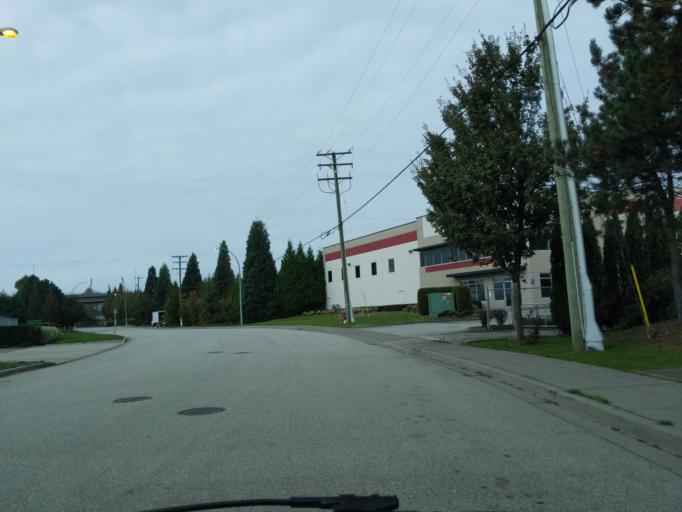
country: CA
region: British Columbia
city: Walnut Grove
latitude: 49.1874
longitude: -122.6604
